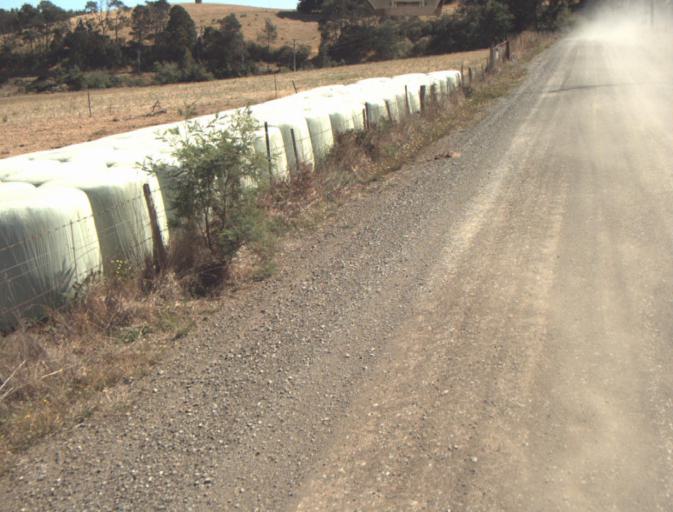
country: AU
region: Tasmania
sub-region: Launceston
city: Mayfield
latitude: -41.2254
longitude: 147.2368
